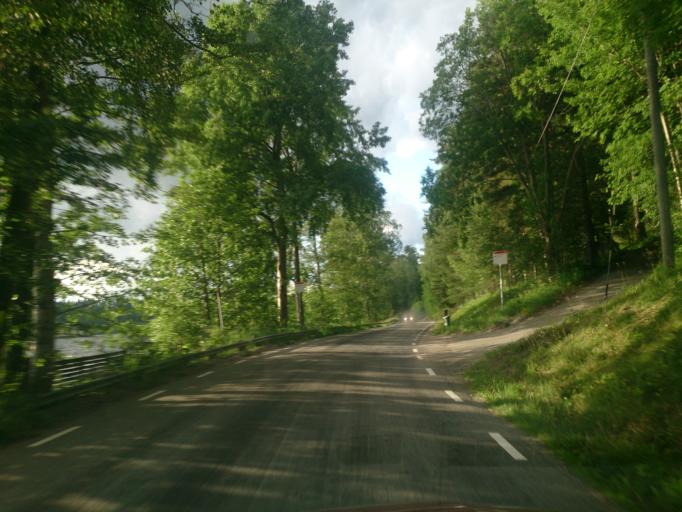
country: SE
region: OEstergoetland
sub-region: Norrkopings Kommun
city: Jursla
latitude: 58.7123
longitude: 16.1540
